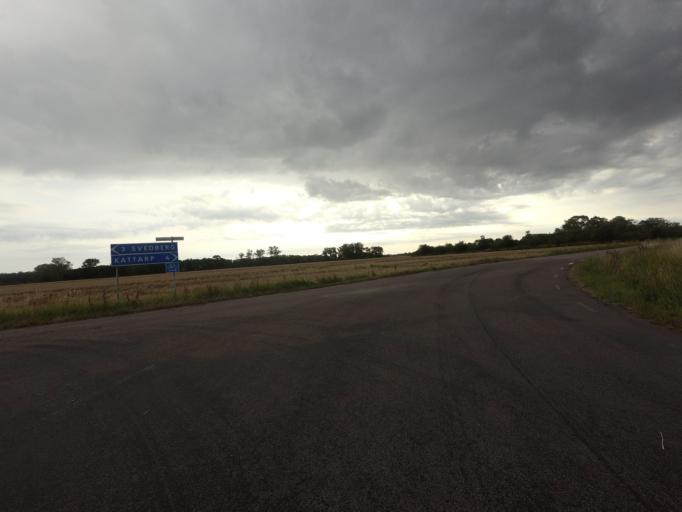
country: SE
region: Skane
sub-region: Helsingborg
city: Odakra
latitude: 56.1410
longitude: 12.7304
